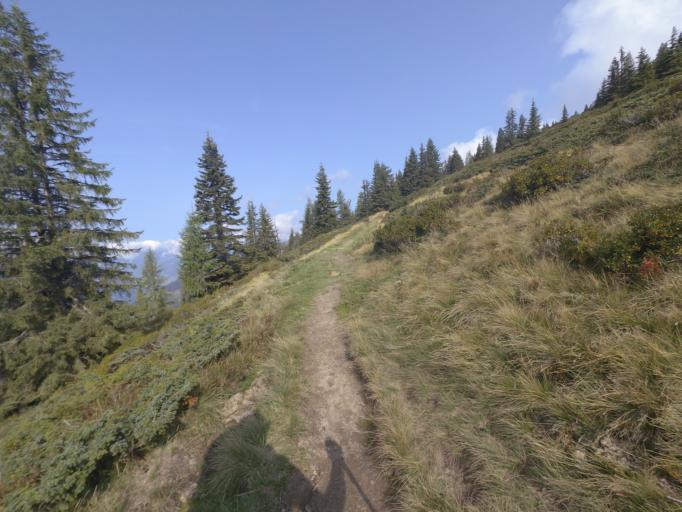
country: AT
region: Salzburg
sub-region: Politischer Bezirk Sankt Johann im Pongau
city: Kleinarl
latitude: 47.2616
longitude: 13.2765
